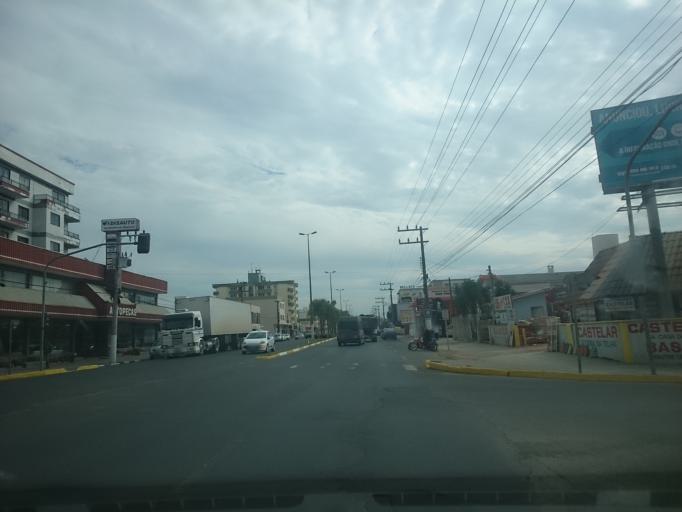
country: BR
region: Santa Catarina
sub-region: Lages
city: Lages
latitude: -27.8023
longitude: -50.3048
